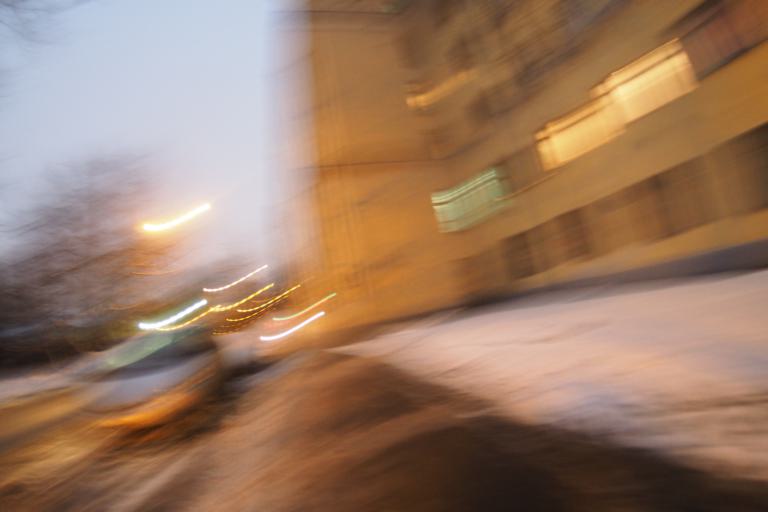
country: RU
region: Moscow
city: Sokol
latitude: 55.7972
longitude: 37.5517
